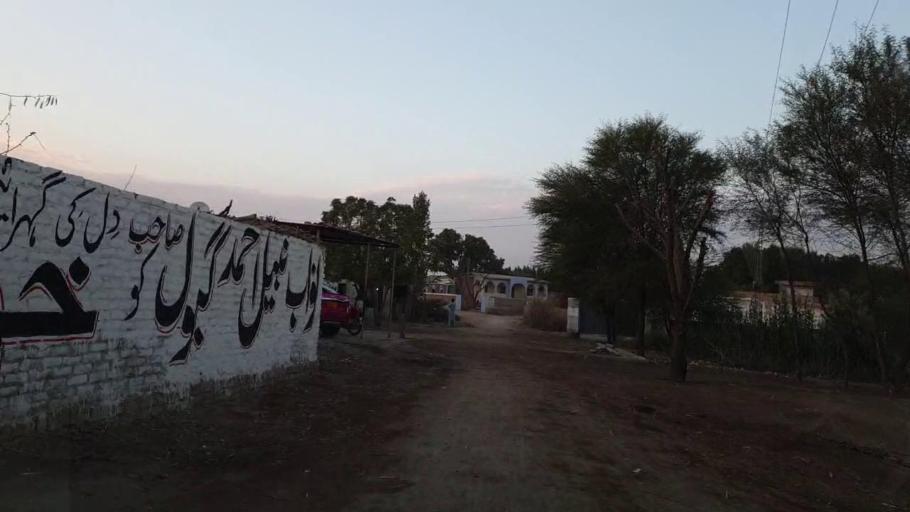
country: PK
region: Sindh
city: Tando Jam
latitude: 25.5046
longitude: 68.5851
